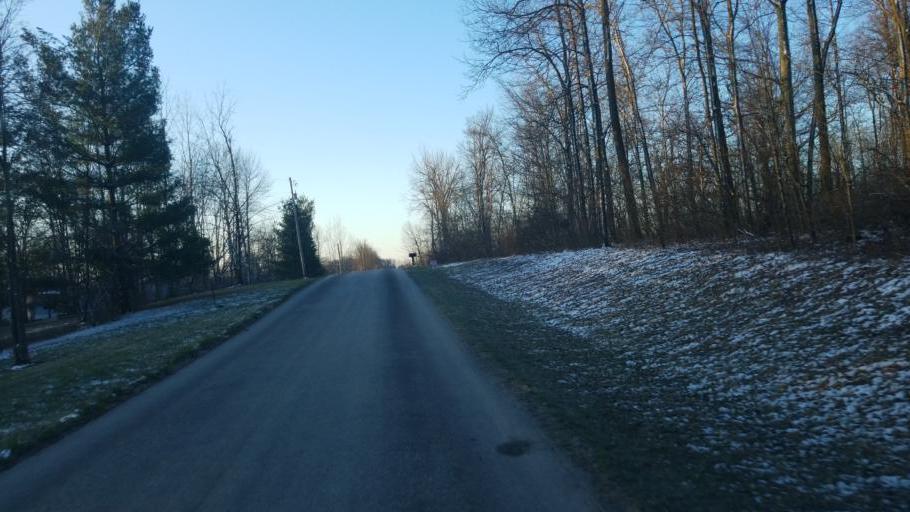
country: US
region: Ohio
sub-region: Highland County
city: Leesburg
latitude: 39.2783
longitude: -83.5021
